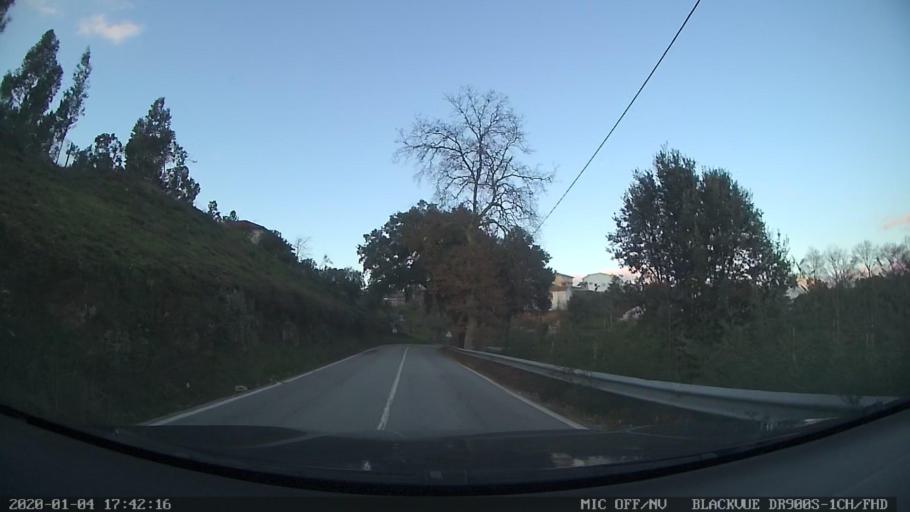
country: PT
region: Braga
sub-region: Cabeceiras de Basto
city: Cabeceiras de Basto
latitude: 41.4698
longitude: -7.9522
